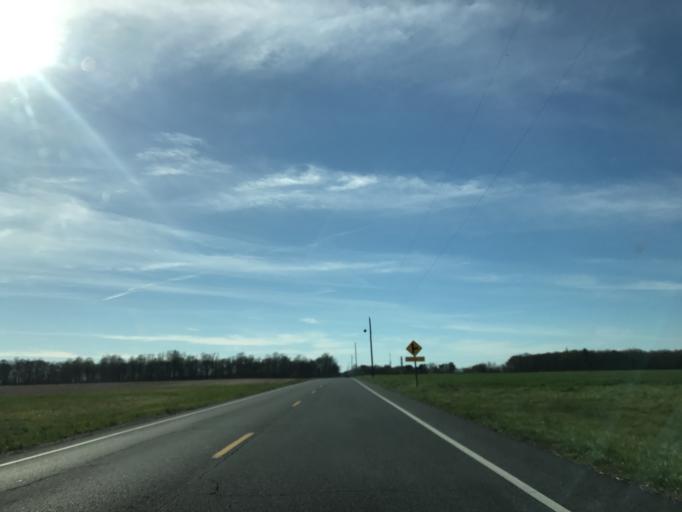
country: US
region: Maryland
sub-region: Caroline County
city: Greensboro
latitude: 39.0320
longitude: -75.7638
